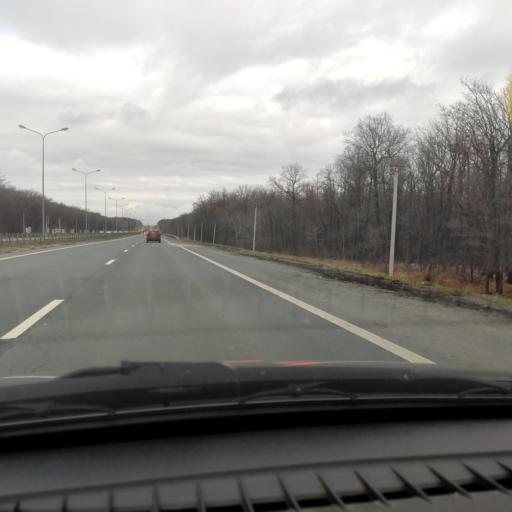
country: RU
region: Samara
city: Novosemeykino
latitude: 53.3466
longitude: 50.3044
